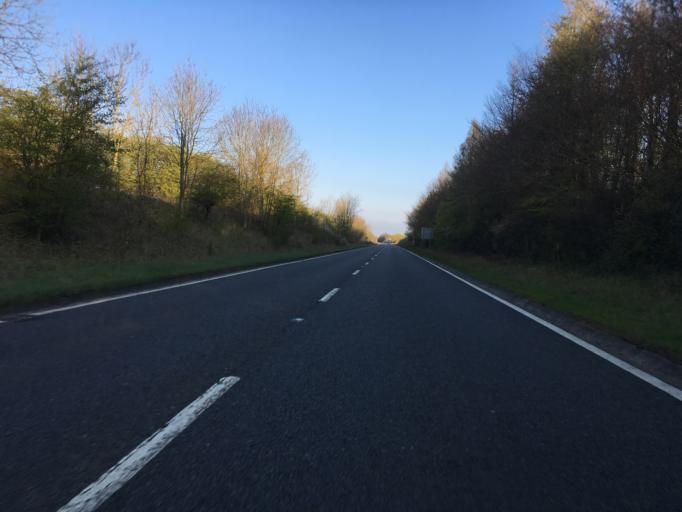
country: GB
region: England
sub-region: Gloucestershire
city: Northleach
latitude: 51.8294
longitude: -1.8138
